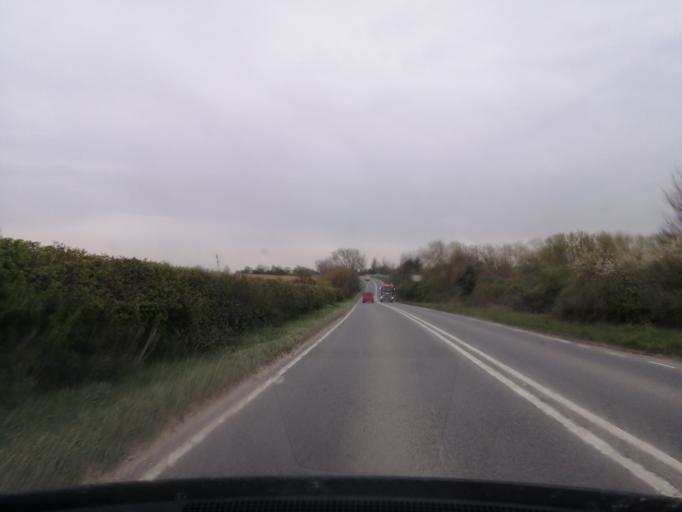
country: GB
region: England
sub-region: Peterborough
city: Thornhaugh
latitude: 52.5875
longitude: -0.4417
